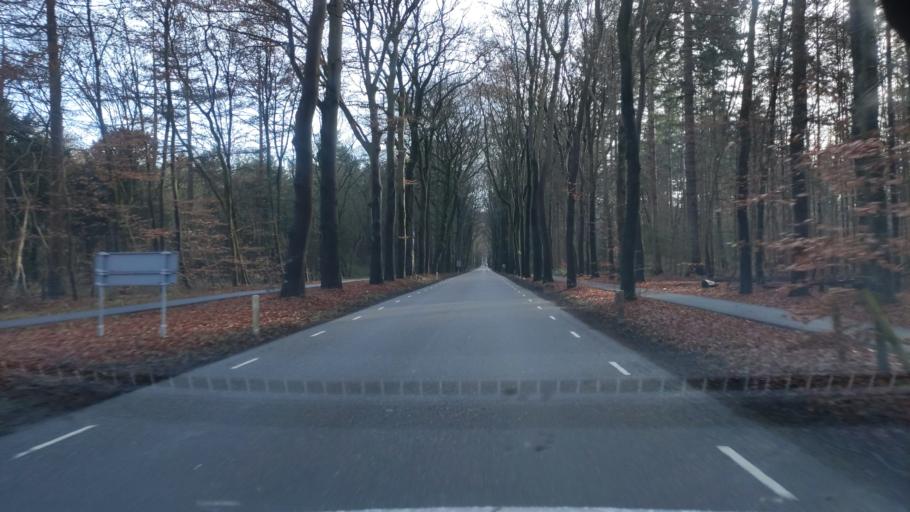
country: NL
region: Gelderland
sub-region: Gemeente Putten
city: Putten
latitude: 52.2503
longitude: 5.6290
